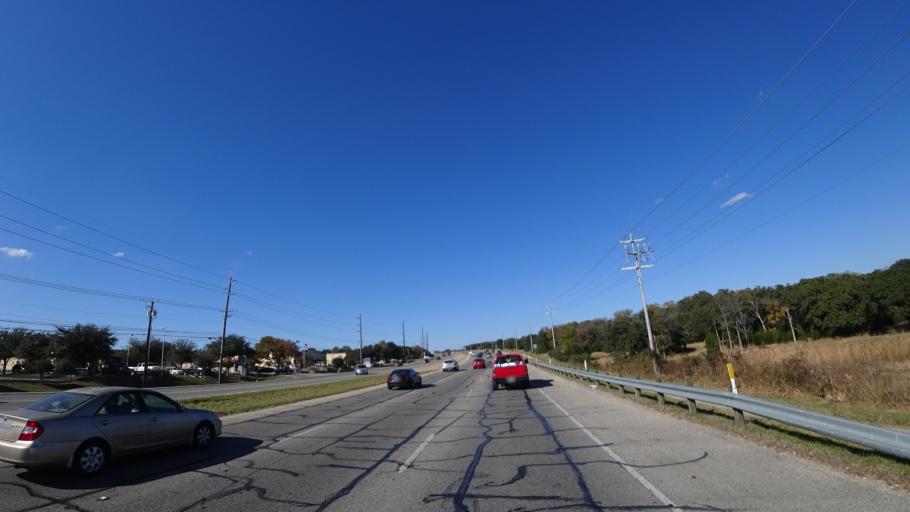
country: US
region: Texas
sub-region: Williamson County
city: Jollyville
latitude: 30.4447
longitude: -97.7427
